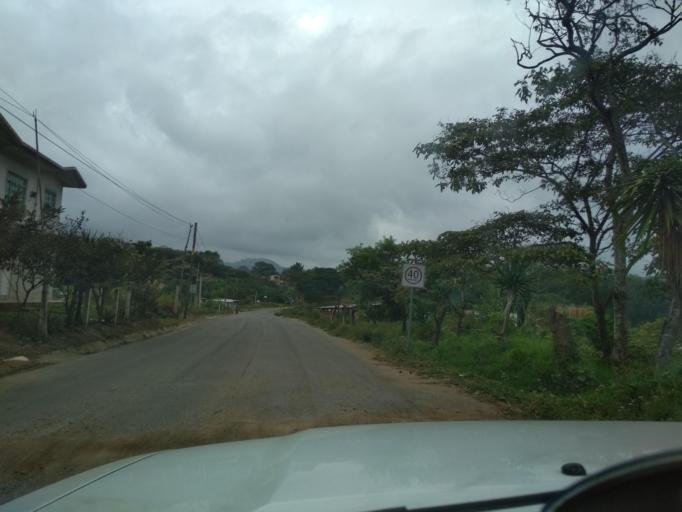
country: MX
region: Veracruz
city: El Castillo
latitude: 19.5484
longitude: -96.8479
